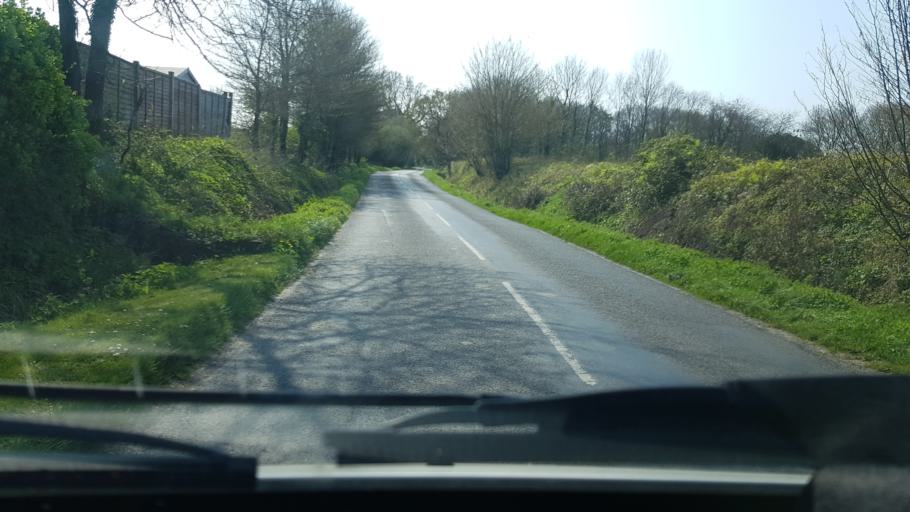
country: GB
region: England
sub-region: West Sussex
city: Chichester
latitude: 50.8251
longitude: -0.8024
